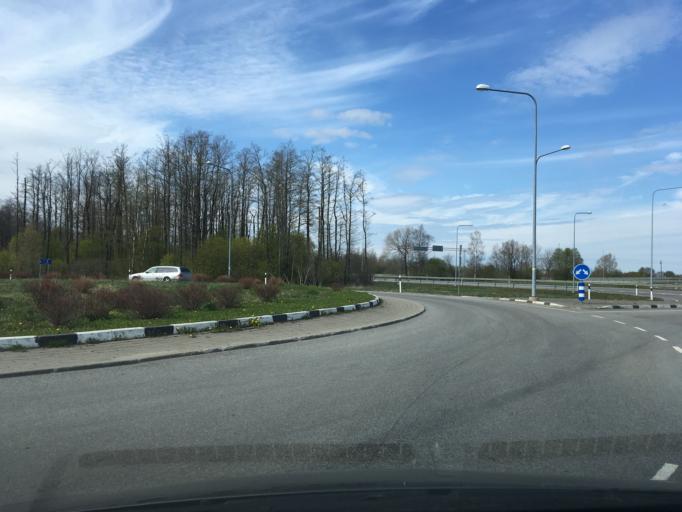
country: EE
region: Harju
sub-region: Joelaehtme vald
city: Loo
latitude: 59.4486
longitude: 24.9767
